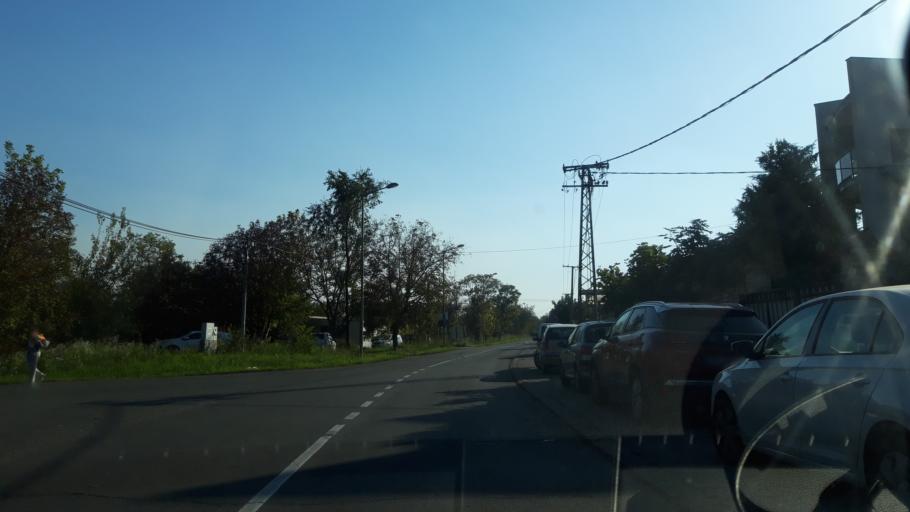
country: RS
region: Autonomna Pokrajina Vojvodina
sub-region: Juznobacki Okrug
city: Petrovaradin
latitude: 45.2411
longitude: 19.8665
